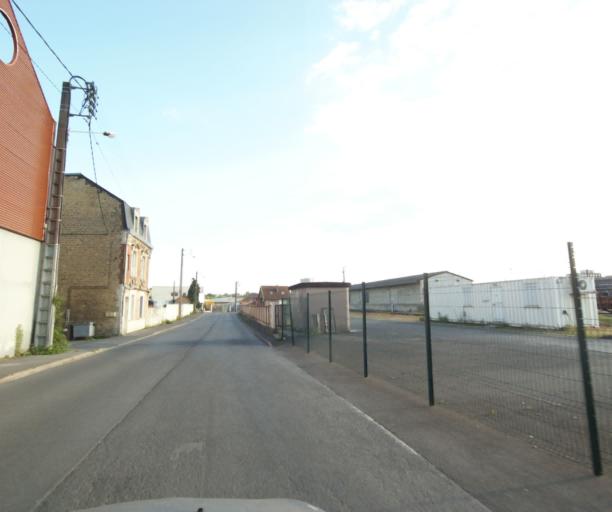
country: FR
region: Champagne-Ardenne
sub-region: Departement des Ardennes
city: Charleville-Mezieres
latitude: 49.7682
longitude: 4.7281
